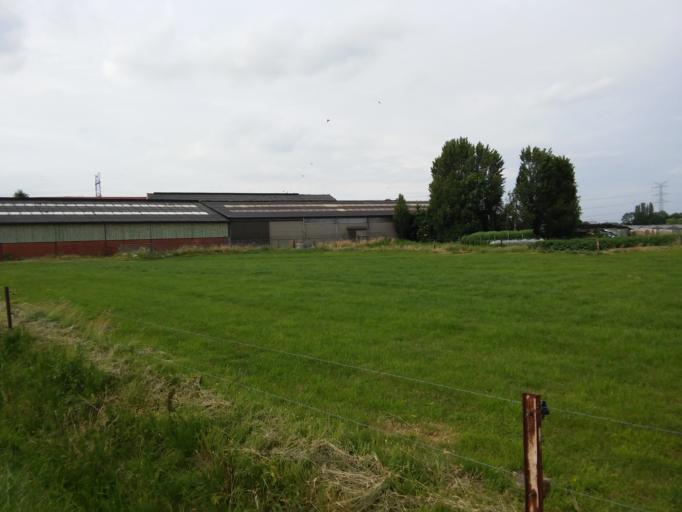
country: BE
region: Flanders
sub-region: Provincie Antwerpen
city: Rumst
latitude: 51.1069
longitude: 4.4111
